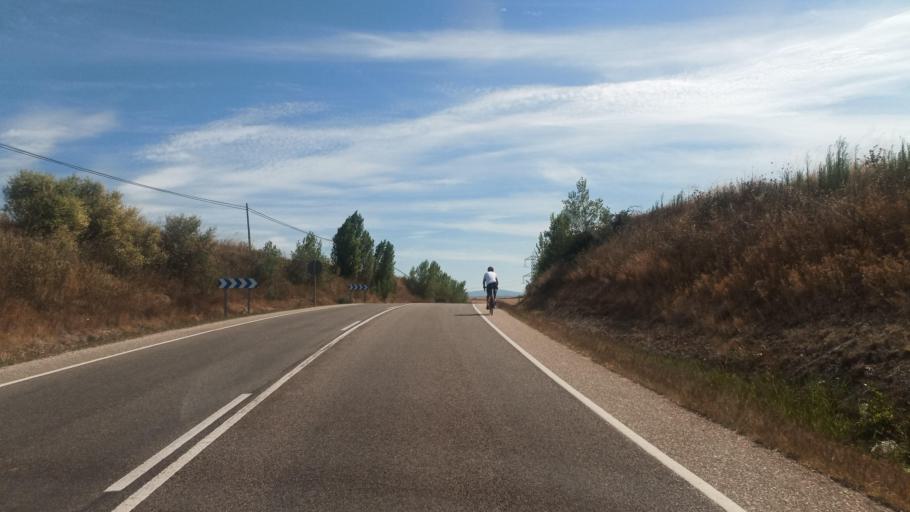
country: ES
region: Castille and Leon
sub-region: Provincia de Burgos
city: Aguilar de Bureba
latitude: 42.5732
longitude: -3.3316
